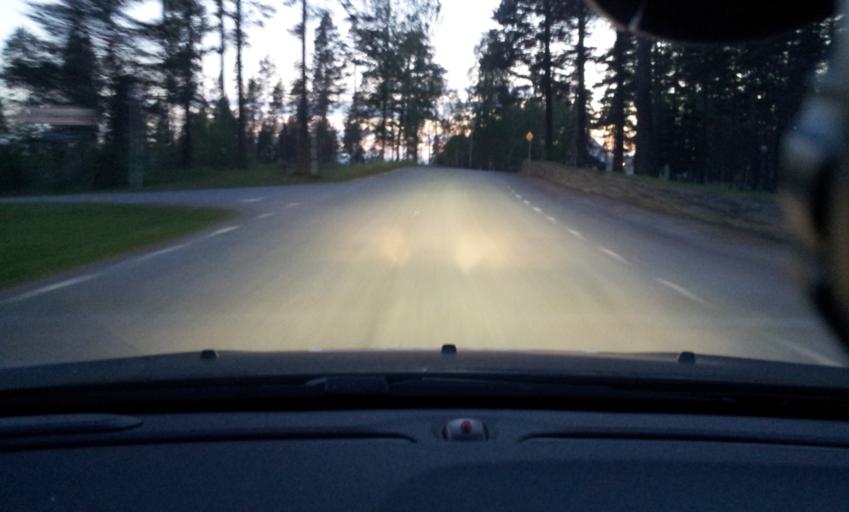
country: SE
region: Jaemtland
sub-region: Braecke Kommun
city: Braecke
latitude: 62.7413
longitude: 15.4349
